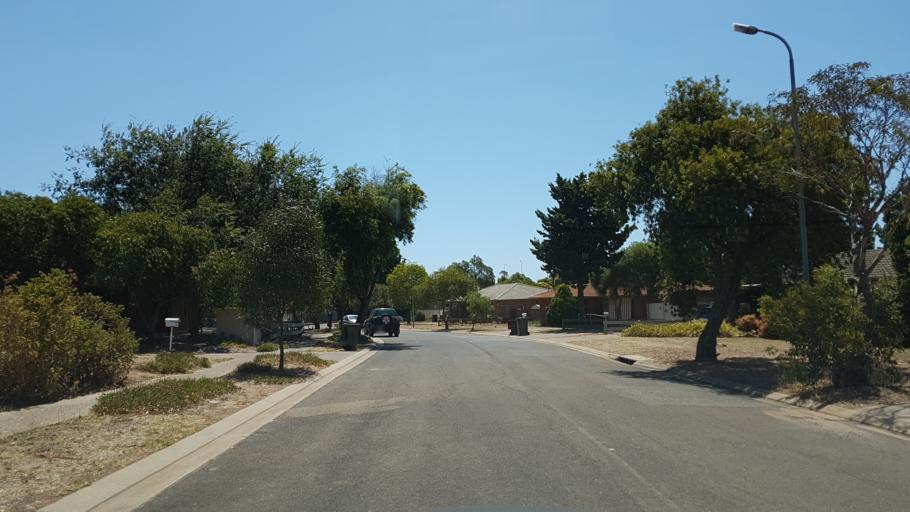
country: AU
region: South Australia
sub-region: Onkaparinga
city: Reynella
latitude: -35.1075
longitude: 138.5127
